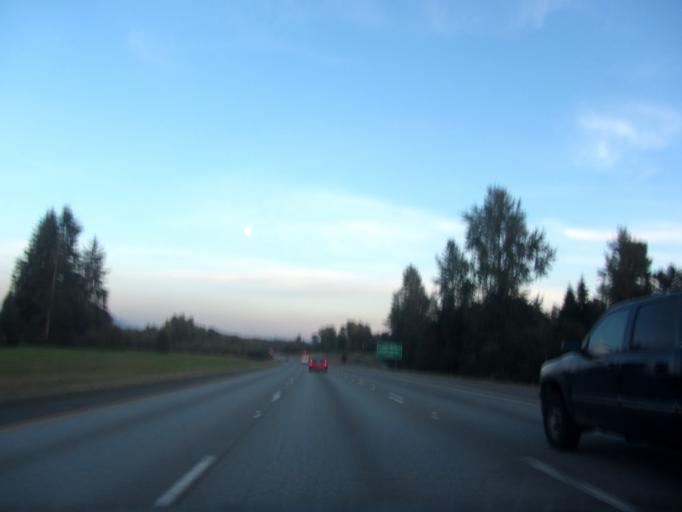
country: US
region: Washington
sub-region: Snohomish County
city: Bryant
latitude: 48.2286
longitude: -122.2311
